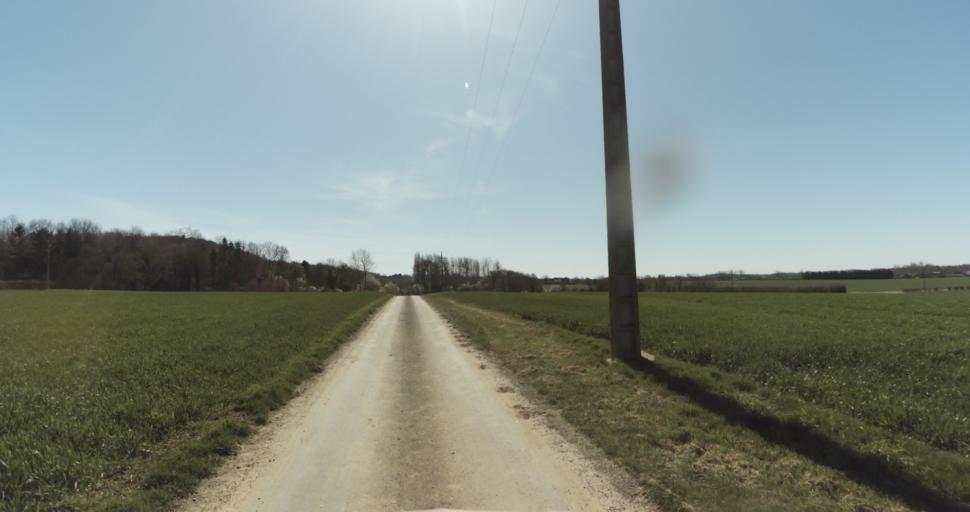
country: FR
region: Lower Normandy
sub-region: Departement du Calvados
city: Saint-Pierre-sur-Dives
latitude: 49.0198
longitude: 0.0319
